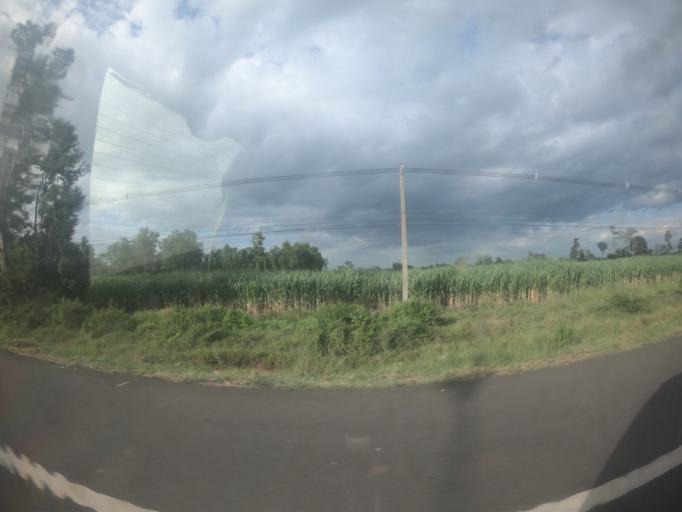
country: TH
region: Surin
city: Kap Choeng
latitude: 14.5237
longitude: 103.5386
